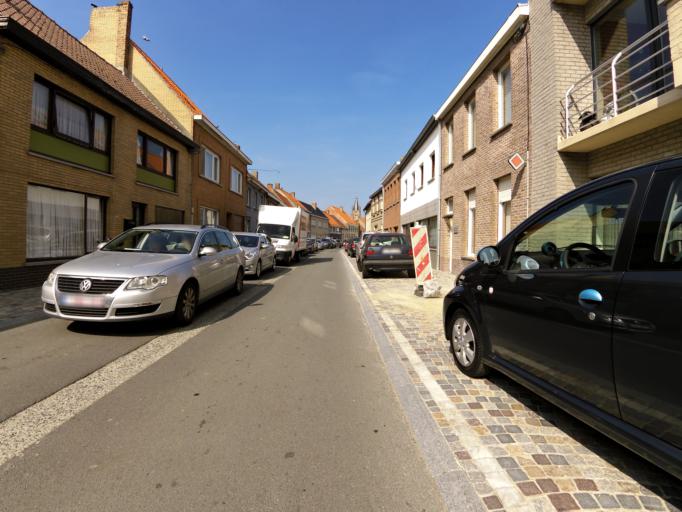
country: BE
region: Flanders
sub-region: Provincie West-Vlaanderen
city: Middelkerke
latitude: 51.1722
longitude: 2.8790
